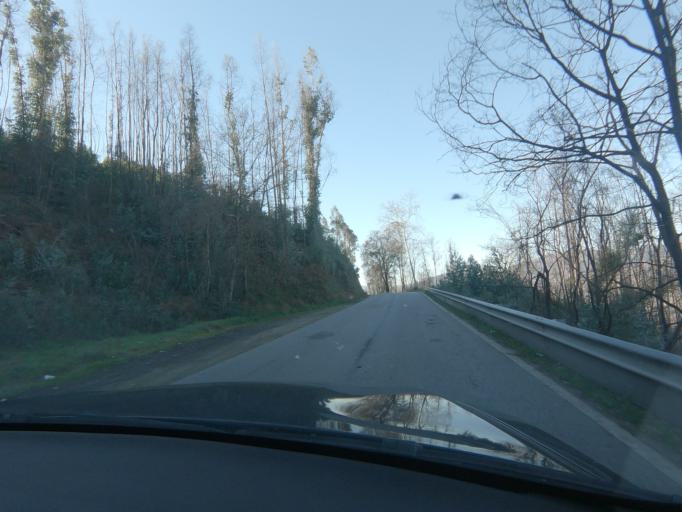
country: PT
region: Viseu
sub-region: Vouzela
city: Vouzela
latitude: 40.7299
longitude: -8.1405
